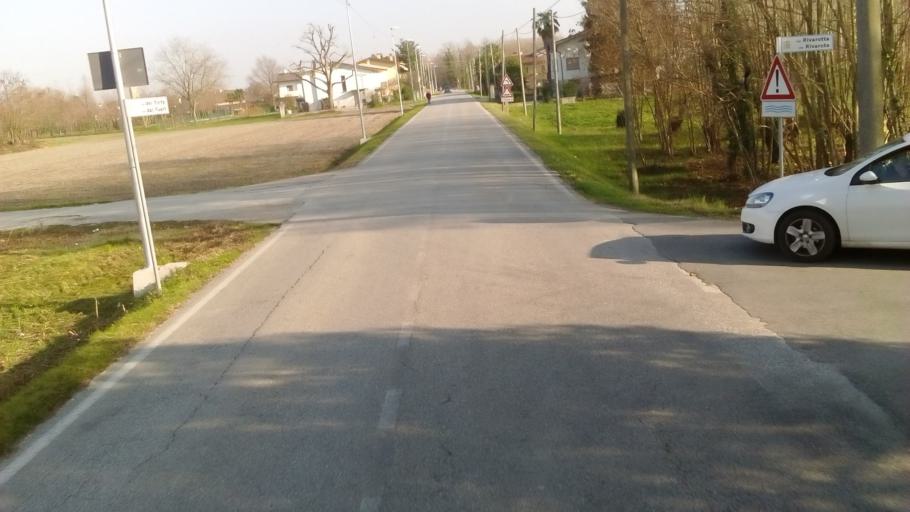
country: IT
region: Friuli Venezia Giulia
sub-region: Provincia di Udine
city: Precenicco
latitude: 45.8124
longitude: 13.0779
